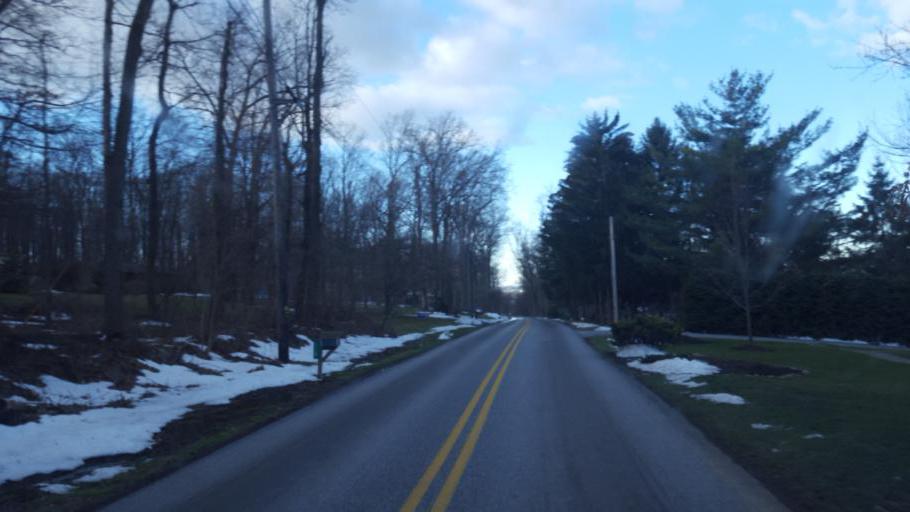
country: US
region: Pennsylvania
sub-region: Lancaster County
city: East Earl
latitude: 40.0743
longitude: -76.0525
